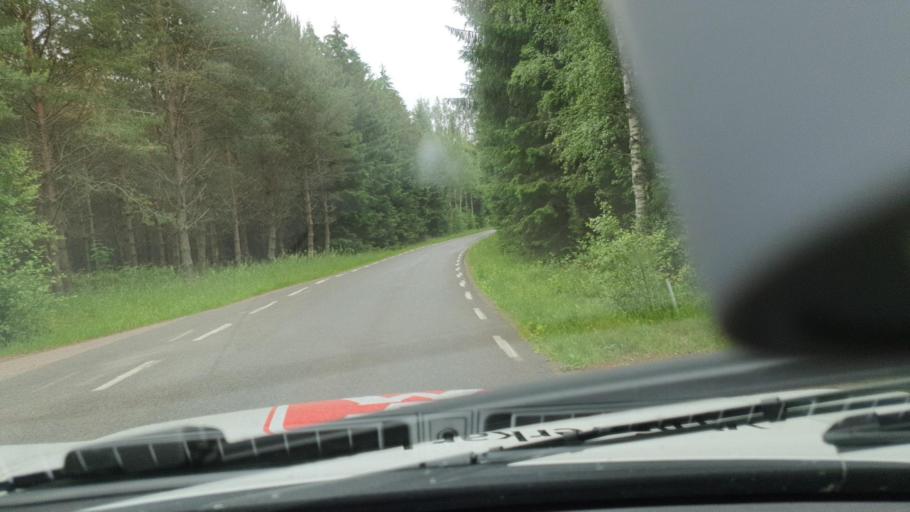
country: SE
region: Vaestra Goetaland
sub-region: Hjo Kommun
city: Hjo
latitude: 58.3204
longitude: 14.1848
